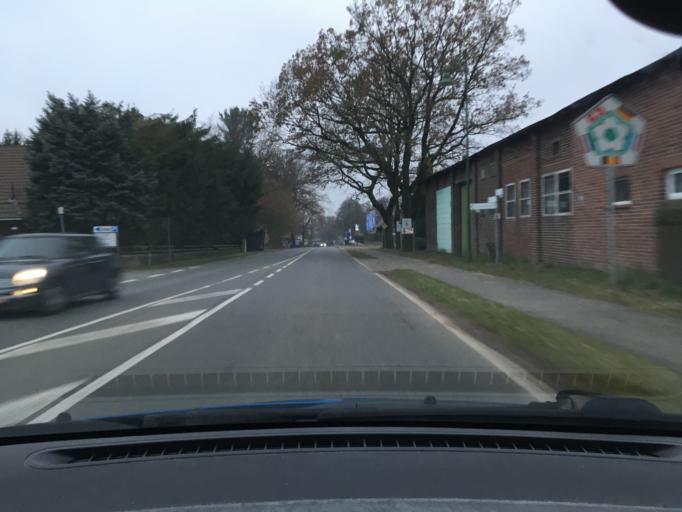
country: DE
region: Lower Saxony
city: Bispingen
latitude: 53.1046
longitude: 9.9716
